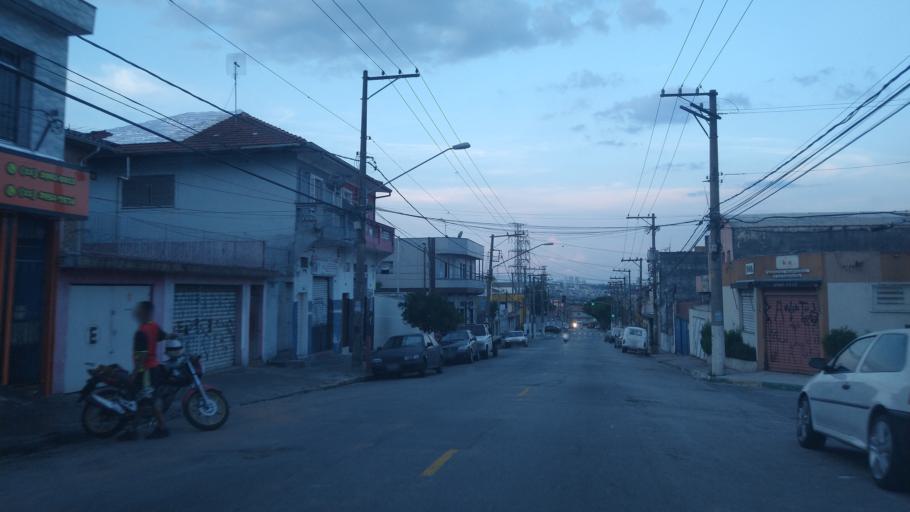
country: BR
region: Sao Paulo
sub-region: Guarulhos
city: Guarulhos
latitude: -23.4914
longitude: -46.5779
